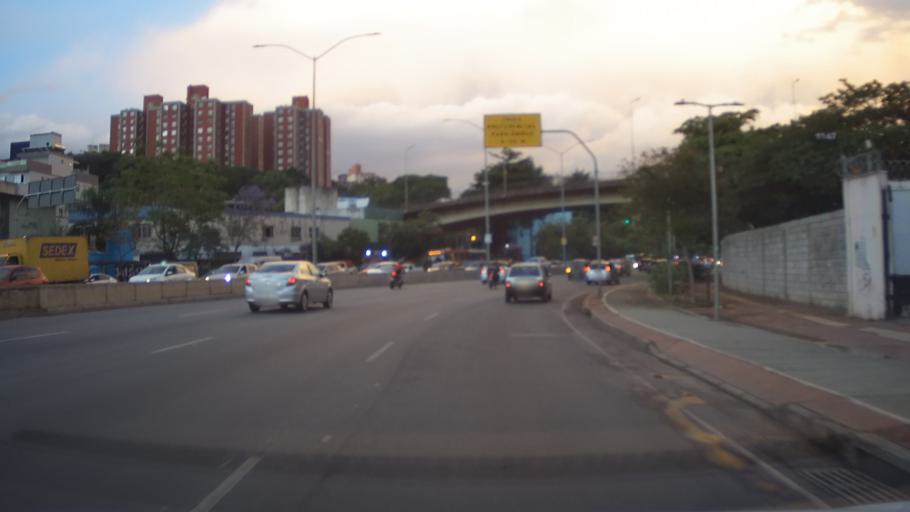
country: BR
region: Minas Gerais
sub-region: Belo Horizonte
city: Belo Horizonte
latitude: -19.9197
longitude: -43.9691
